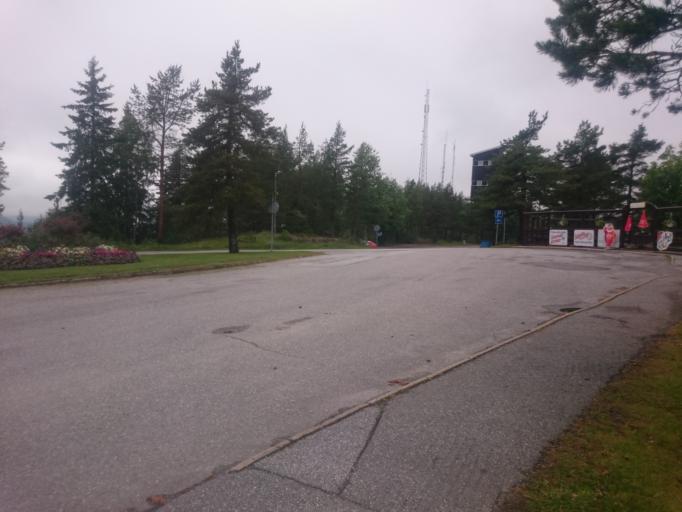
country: SE
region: Vaesternorrland
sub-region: OErnskoeldsviks Kommun
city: Ornskoldsvik
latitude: 63.2879
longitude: 18.6964
